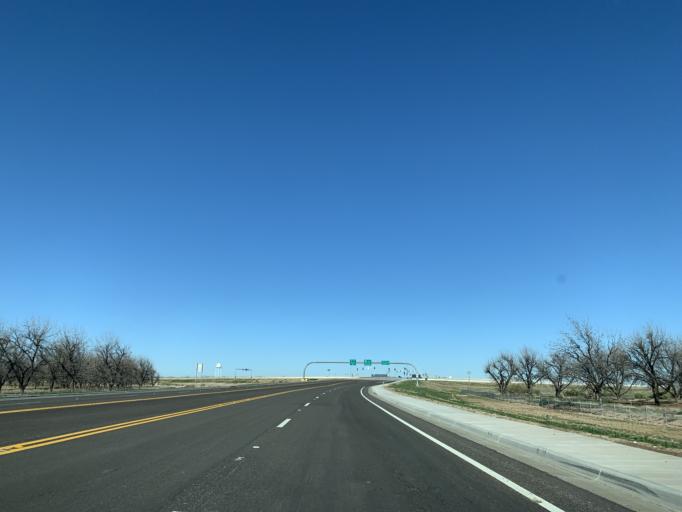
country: US
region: Arizona
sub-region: Pinal County
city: Eloy
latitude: 32.7211
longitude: -111.5174
